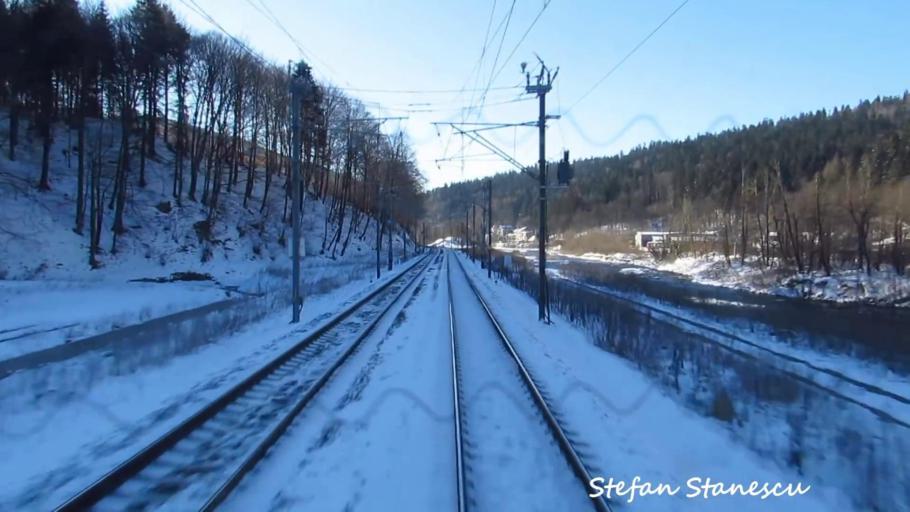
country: RO
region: Prahova
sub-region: Oras Busteni
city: Poiana Tapului
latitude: 45.3740
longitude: 25.5431
